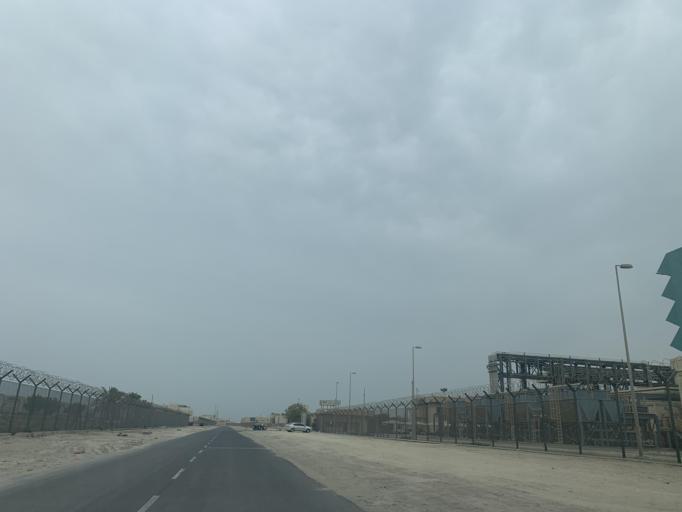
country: BH
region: Muharraq
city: Al Hadd
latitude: 26.2192
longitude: 50.6592
